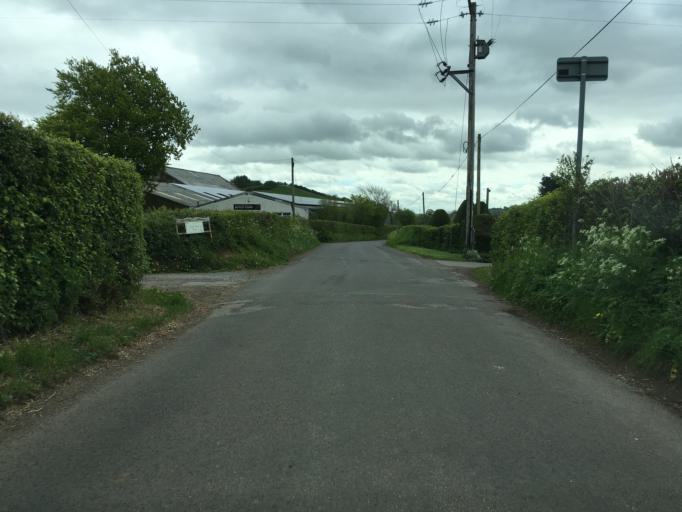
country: GB
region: England
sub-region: Bath and North East Somerset
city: Clutton
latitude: 51.3373
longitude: -2.5228
